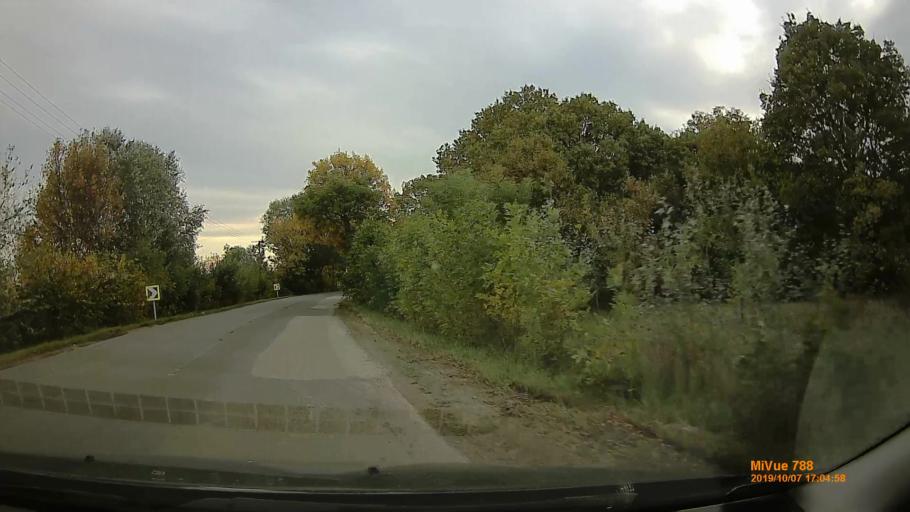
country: HU
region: Bekes
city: Szarvas
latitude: 46.8287
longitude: 20.5420
